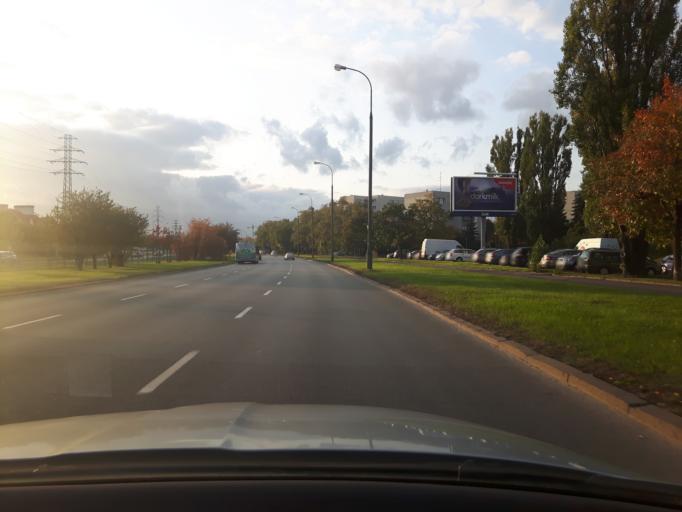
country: PL
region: Masovian Voivodeship
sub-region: Warszawa
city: Ursynow
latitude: 52.1503
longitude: 21.0311
